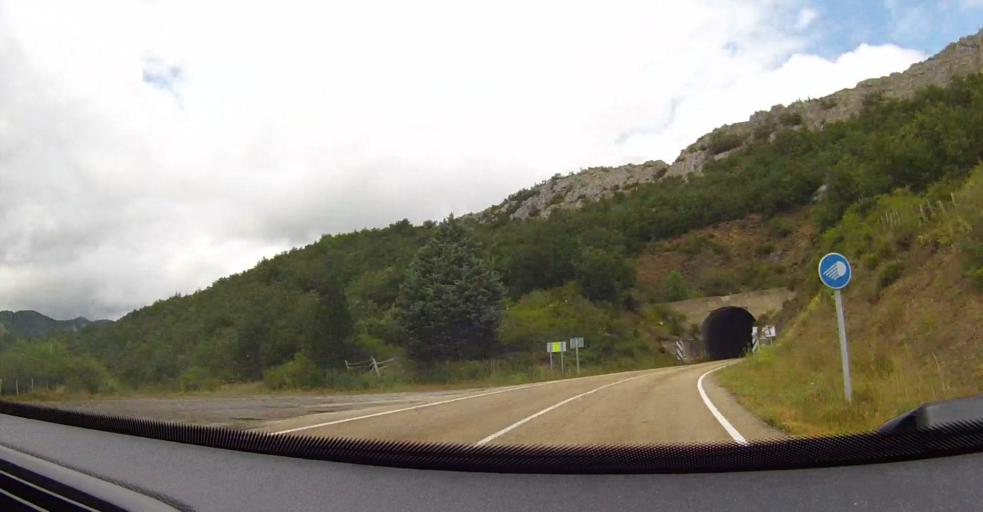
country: ES
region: Castille and Leon
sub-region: Provincia de Leon
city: Puebla de Lillo
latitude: 42.9686
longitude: -5.2569
